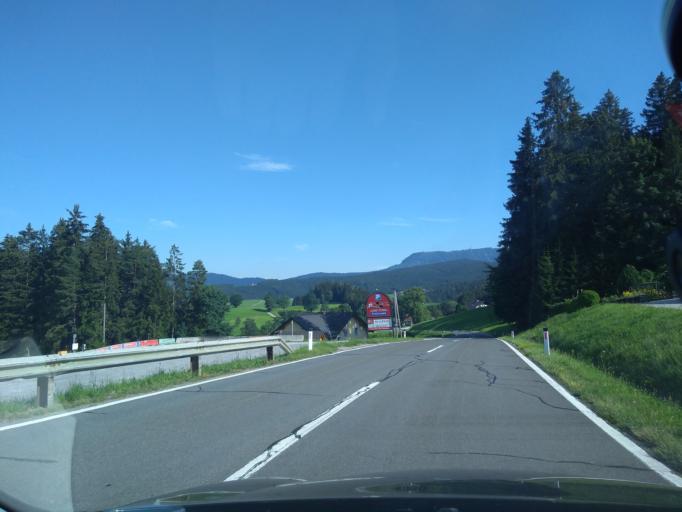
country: AT
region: Styria
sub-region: Politischer Bezirk Graz-Umgebung
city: Semriach
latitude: 47.2694
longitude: 15.4253
